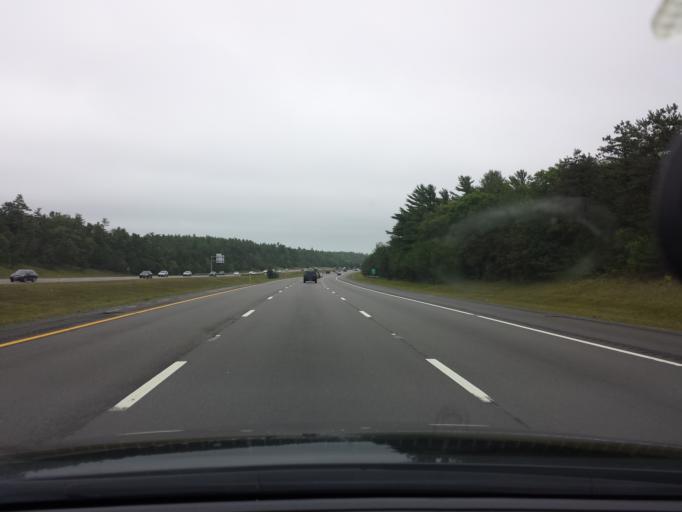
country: US
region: Massachusetts
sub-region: Plymouth County
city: White Island Shores
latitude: 41.7722
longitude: -70.6415
